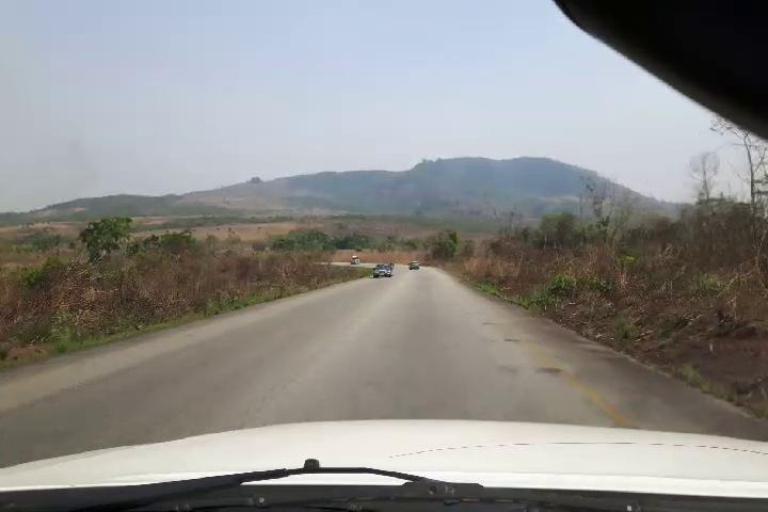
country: SL
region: Northern Province
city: Yonibana
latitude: 8.3871
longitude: -12.1919
